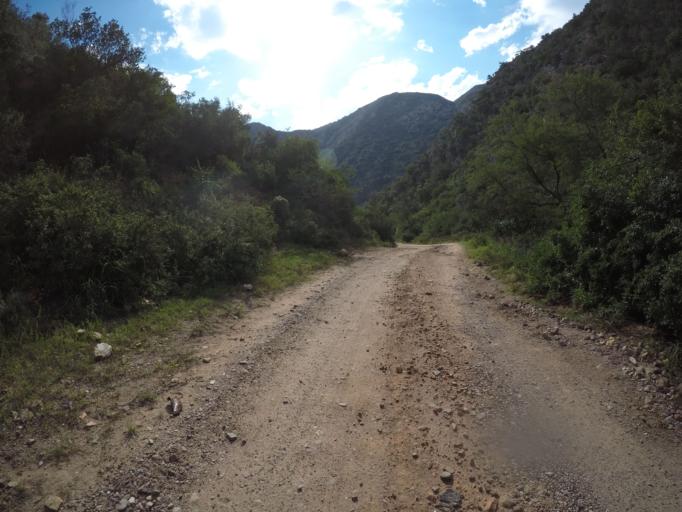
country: ZA
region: Eastern Cape
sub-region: Cacadu District Municipality
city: Kareedouw
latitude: -33.6383
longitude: 24.3224
